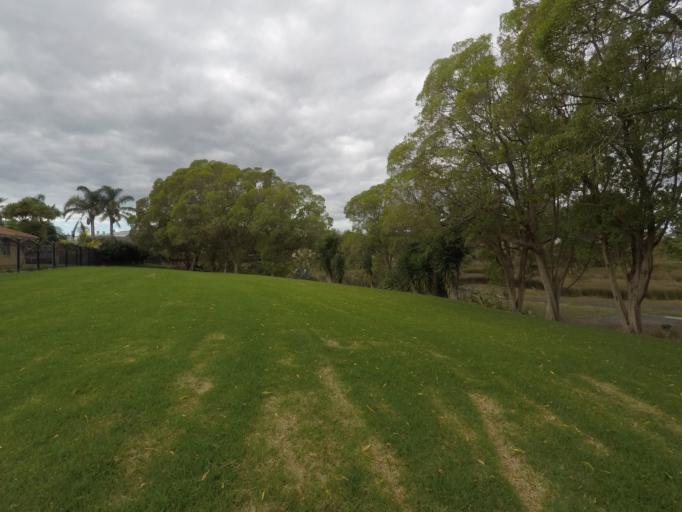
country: NZ
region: Auckland
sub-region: Auckland
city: Papakura
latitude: -37.0534
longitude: 174.9259
